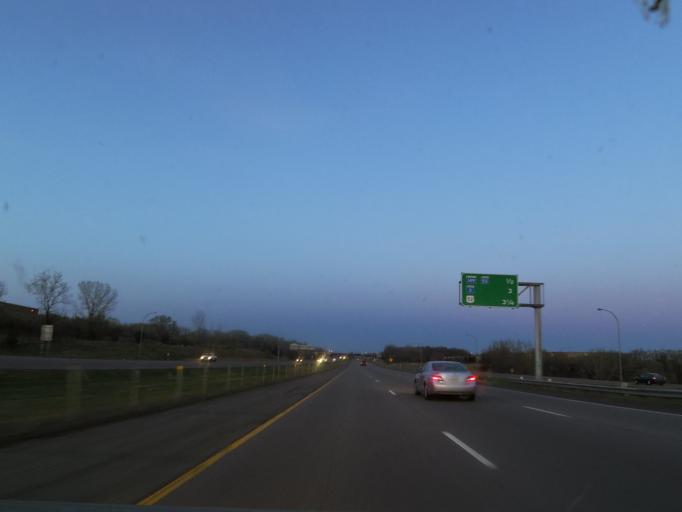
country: US
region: Minnesota
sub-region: Dakota County
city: Mendota Heights
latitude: 44.8627
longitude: -93.1398
